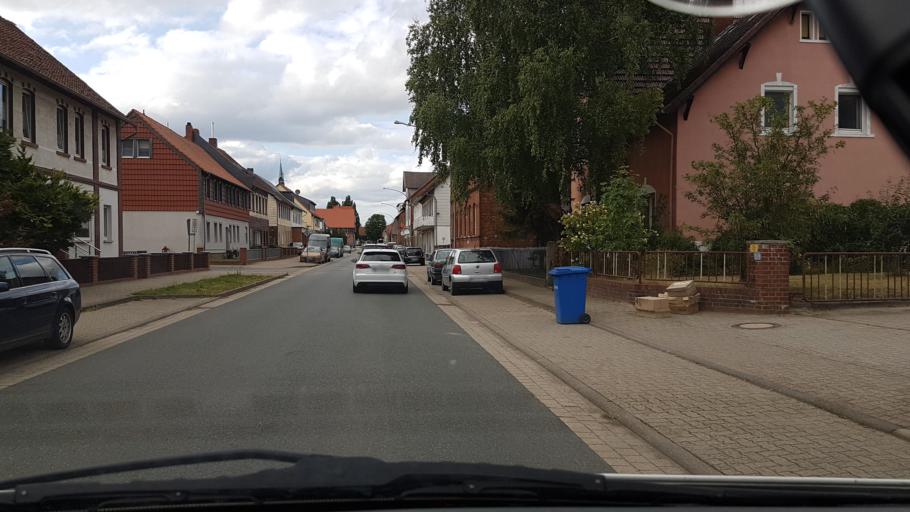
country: DE
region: Lower Saxony
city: Supplingen
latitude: 52.2236
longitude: 10.9061
